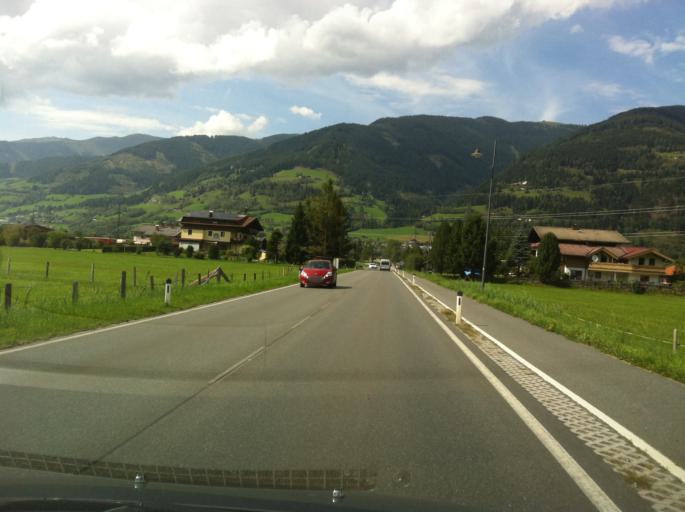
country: AT
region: Salzburg
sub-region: Politischer Bezirk Zell am See
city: Kaprun
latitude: 47.2794
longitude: 12.7563
